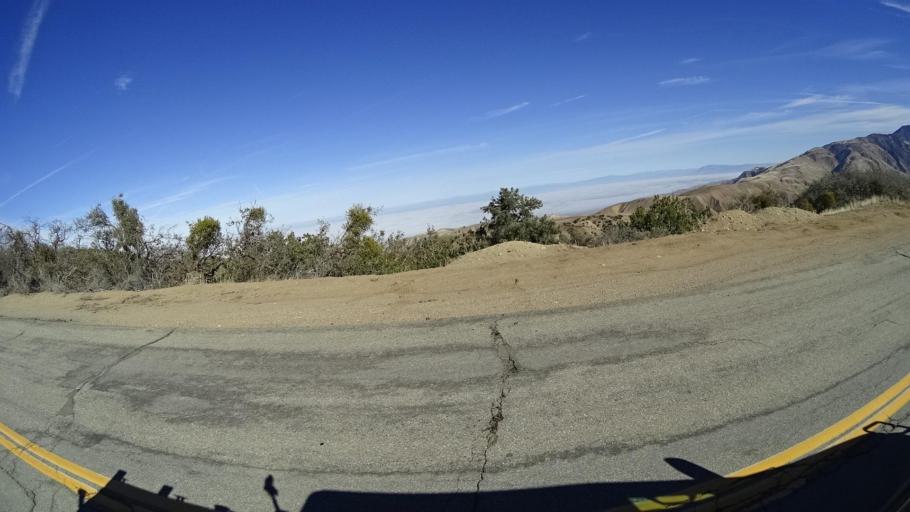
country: US
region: California
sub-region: Kern County
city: Maricopa
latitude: 34.8946
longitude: -119.3625
